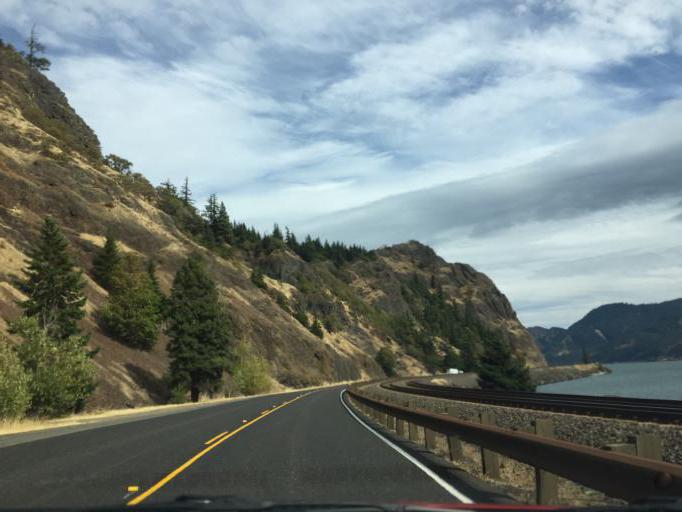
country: US
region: Washington
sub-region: Skamania County
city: Carson
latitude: 45.7101
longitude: -121.6750
